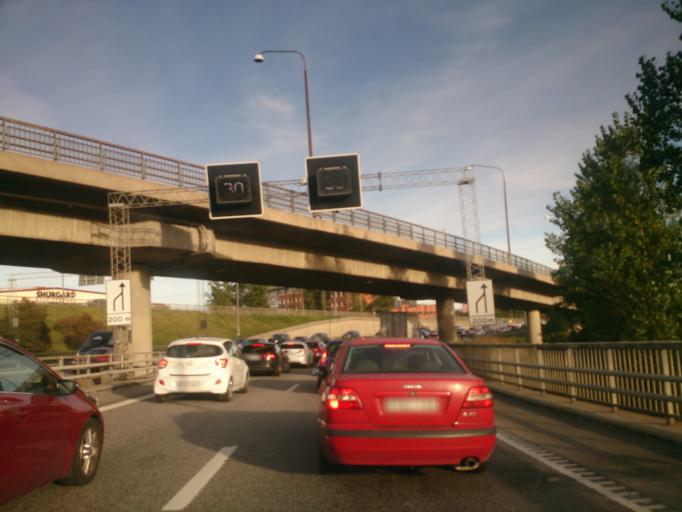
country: SE
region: Stockholm
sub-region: Stockholms Kommun
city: Arsta
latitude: 59.3010
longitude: 18.0217
